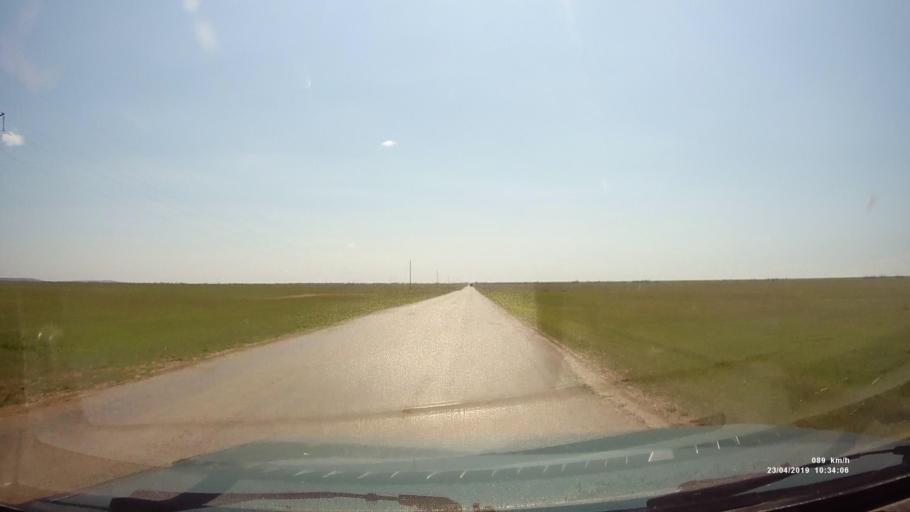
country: RU
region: Kalmykiya
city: Yashalta
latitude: 46.5672
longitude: 42.6060
